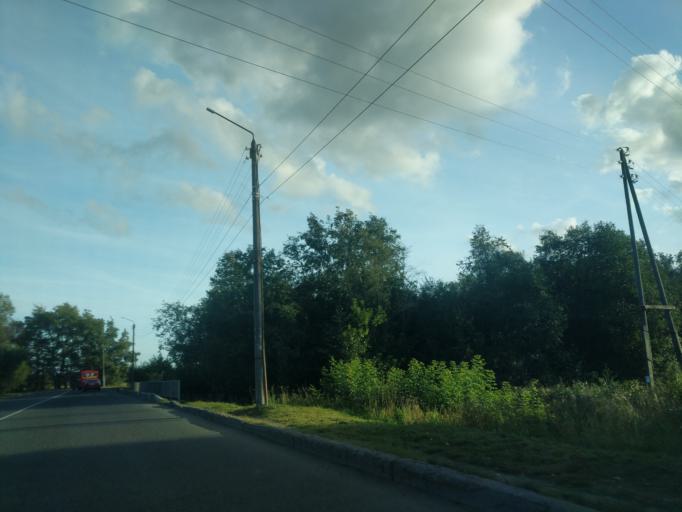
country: RU
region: Kirov
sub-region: Kirovo-Chepetskiy Rayon
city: Kirov
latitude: 58.6159
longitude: 49.7673
